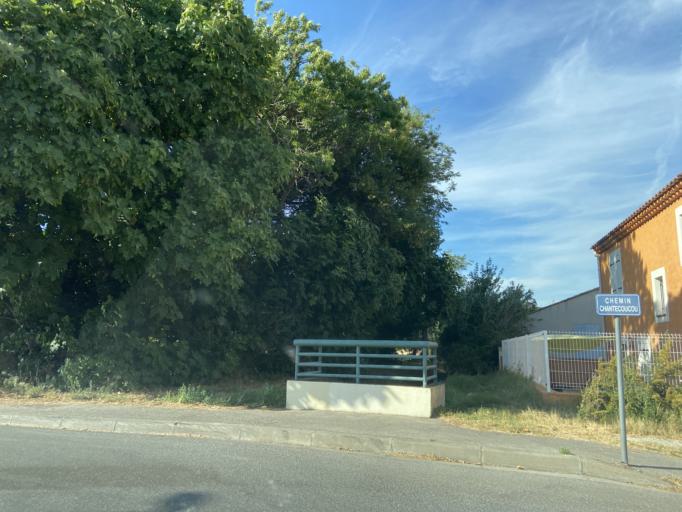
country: FR
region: Provence-Alpes-Cote d'Azur
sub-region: Departement des Bouches-du-Rhone
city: Miramas
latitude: 43.5799
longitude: 5.0085
